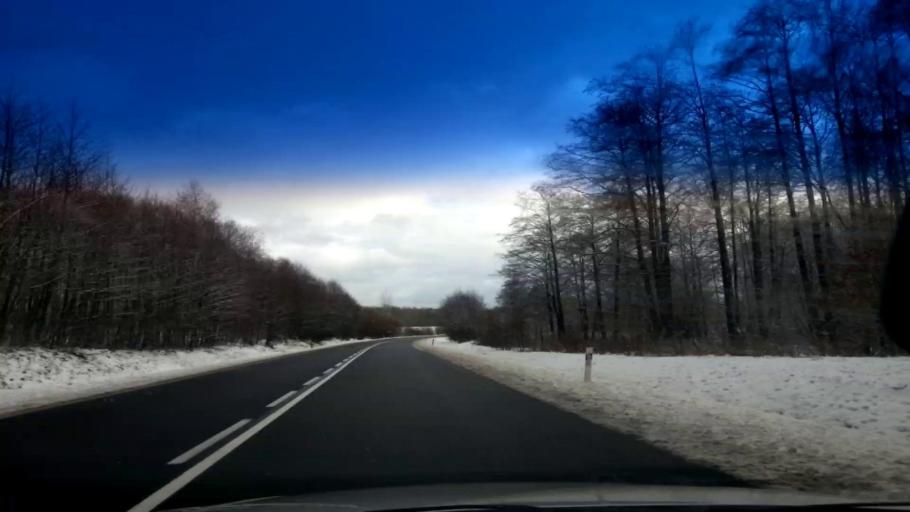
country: CZ
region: Karlovarsky
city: As
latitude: 50.2070
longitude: 12.1892
